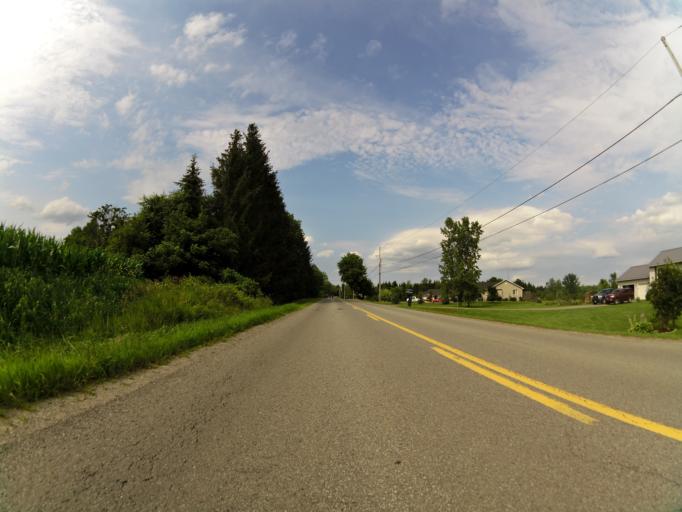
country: CA
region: Ontario
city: Bells Corners
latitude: 45.0547
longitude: -75.6122
